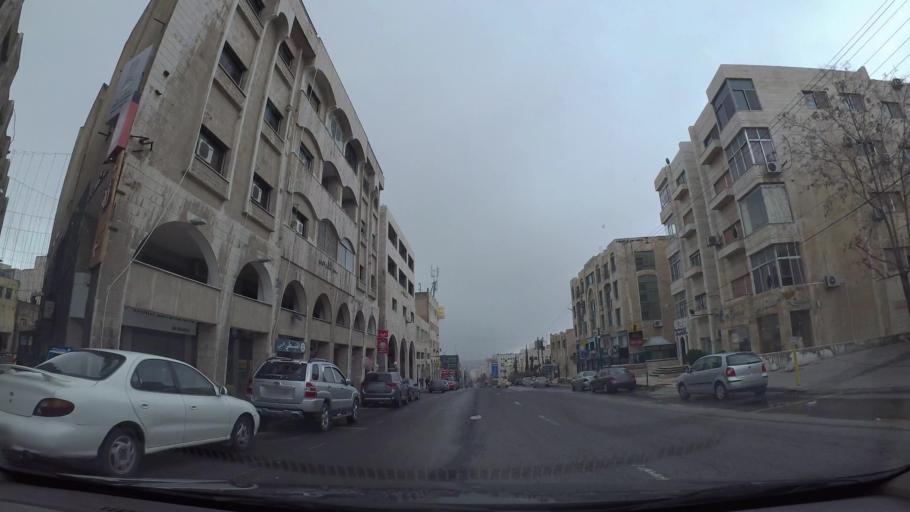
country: JO
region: Amman
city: Wadi as Sir
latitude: 31.9591
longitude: 35.8674
